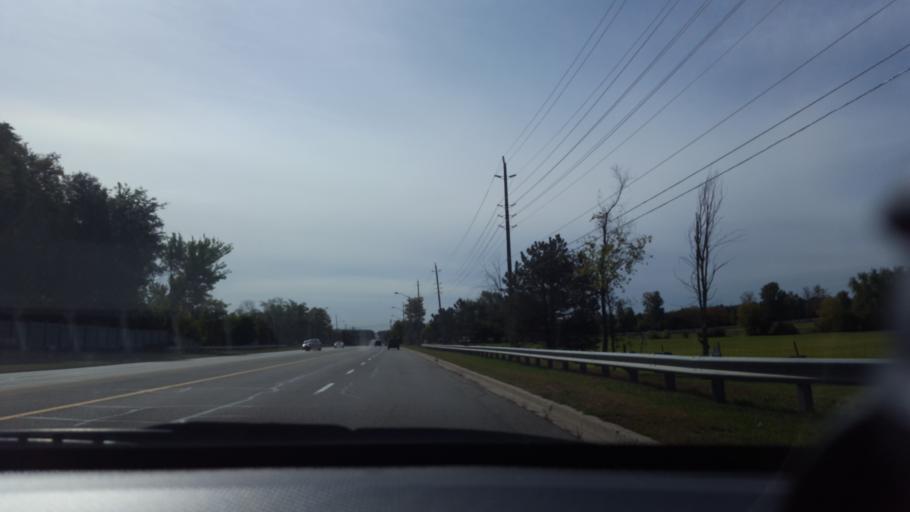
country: CA
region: Ontario
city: Newmarket
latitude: 44.0039
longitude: -79.4966
